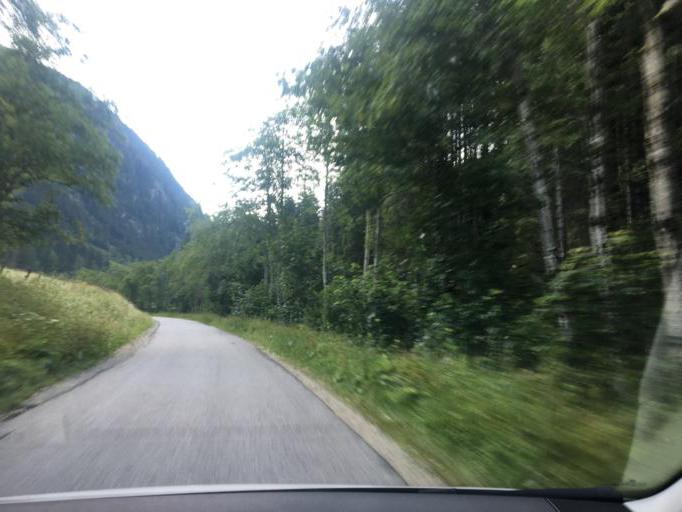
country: AT
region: Styria
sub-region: Politischer Bezirk Liezen
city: Schladming
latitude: 47.3358
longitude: 13.6806
